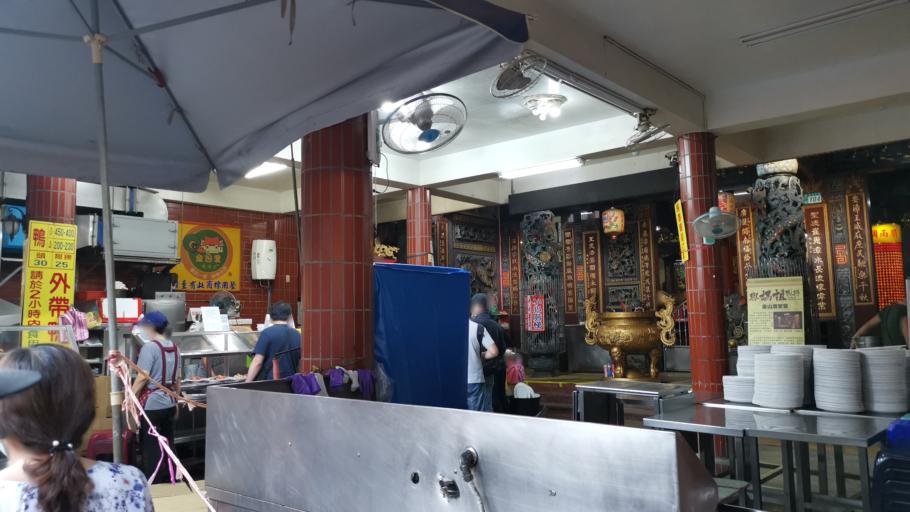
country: TW
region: Taiwan
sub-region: Keelung
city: Keelung
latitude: 25.2219
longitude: 121.6383
